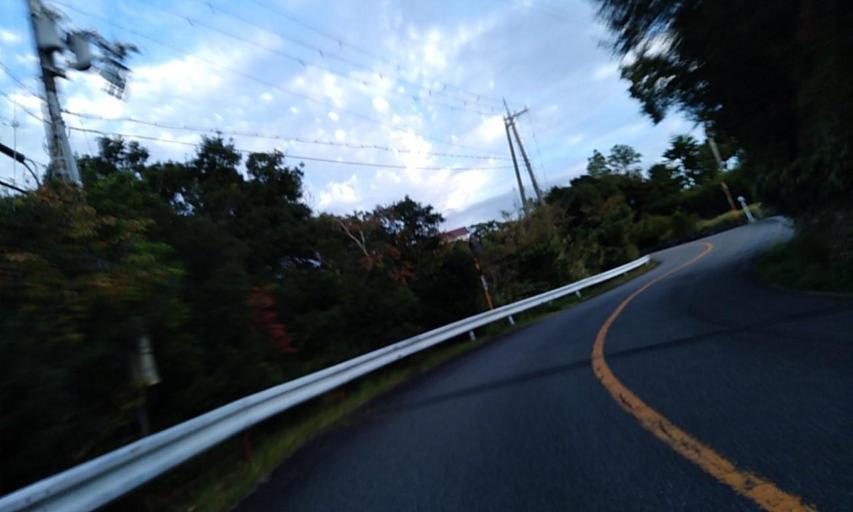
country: JP
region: Wakayama
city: Tanabe
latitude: 33.6642
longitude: 135.3455
